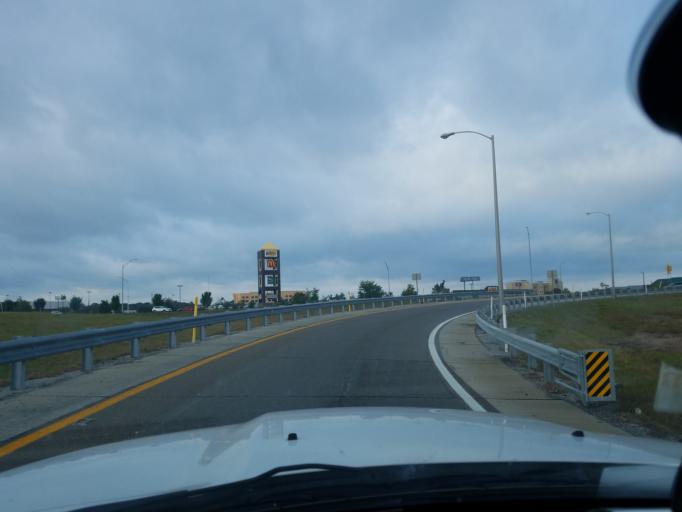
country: US
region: Kentucky
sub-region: Jefferson County
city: Douglass Hills
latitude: 38.2223
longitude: -85.5375
